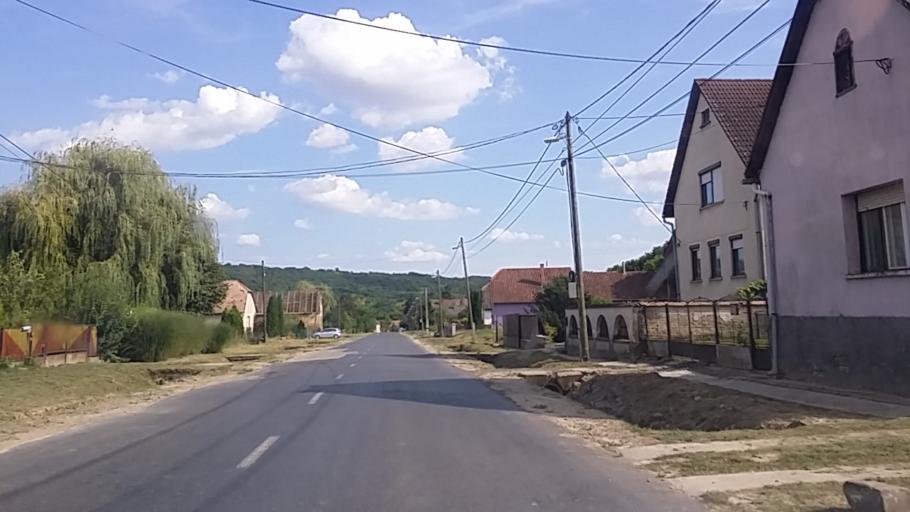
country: HU
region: Tolna
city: Zomba
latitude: 46.5055
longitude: 18.5601
